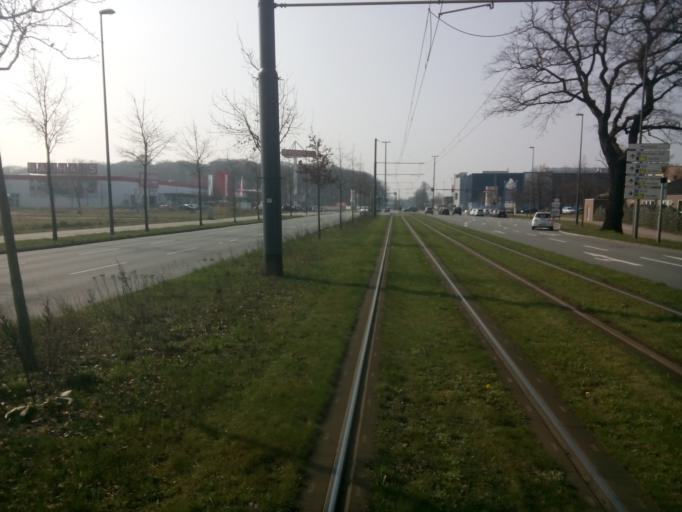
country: DE
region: Lower Saxony
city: Oyten
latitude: 53.0542
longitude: 8.9625
